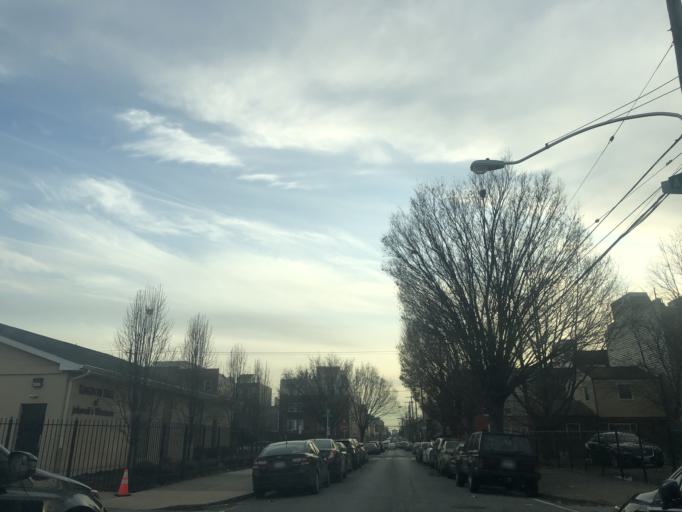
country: US
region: Pennsylvania
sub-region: Philadelphia County
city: Philadelphia
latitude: 39.9389
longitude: -75.1783
